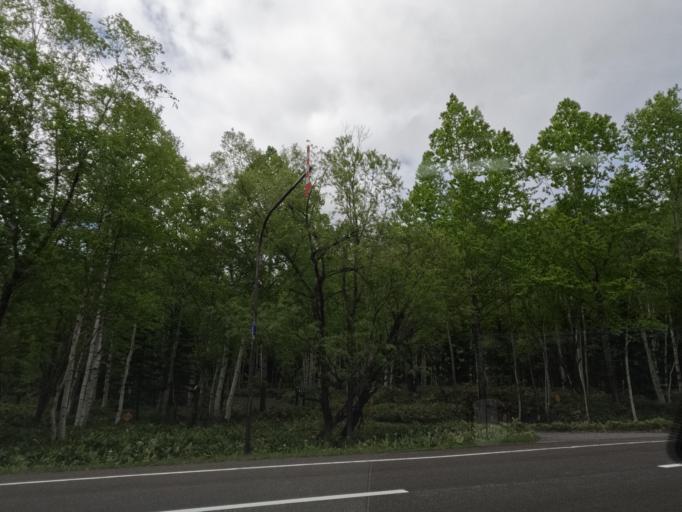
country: JP
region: Hokkaido
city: Kamikawa
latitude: 43.6431
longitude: 143.0186
